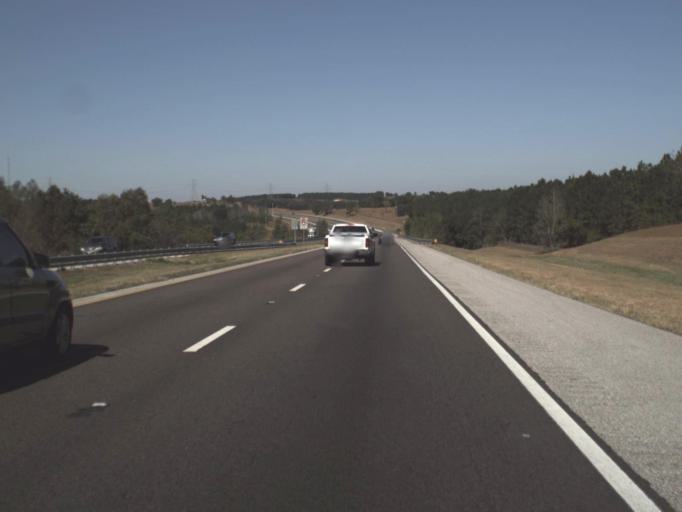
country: US
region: Florida
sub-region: Lake County
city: Minneola
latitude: 28.6038
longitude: -81.7227
